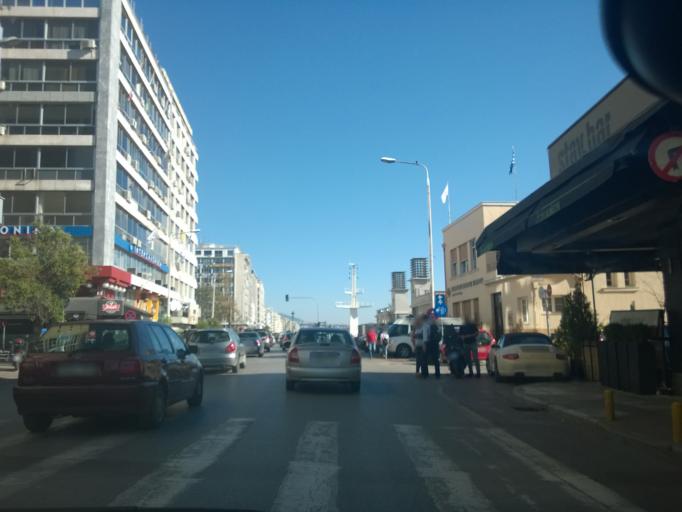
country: GR
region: Central Macedonia
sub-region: Nomos Thessalonikis
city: Thessaloniki
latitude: 40.6342
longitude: 22.9364
